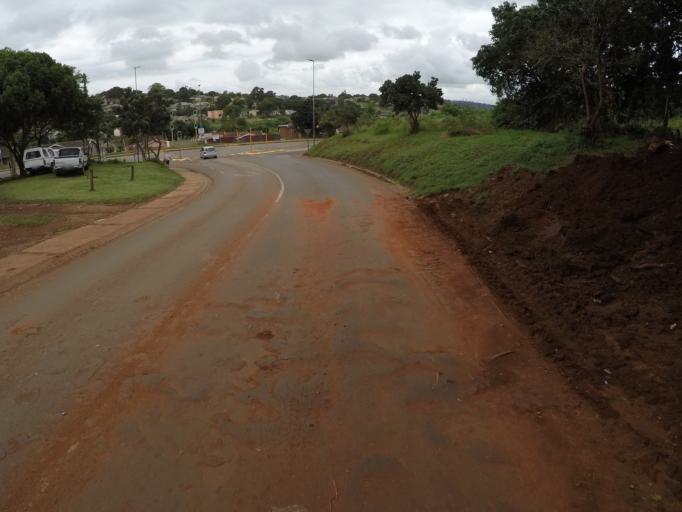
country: ZA
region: KwaZulu-Natal
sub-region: uThungulu District Municipality
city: Empangeni
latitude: -28.7743
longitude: 31.8655
